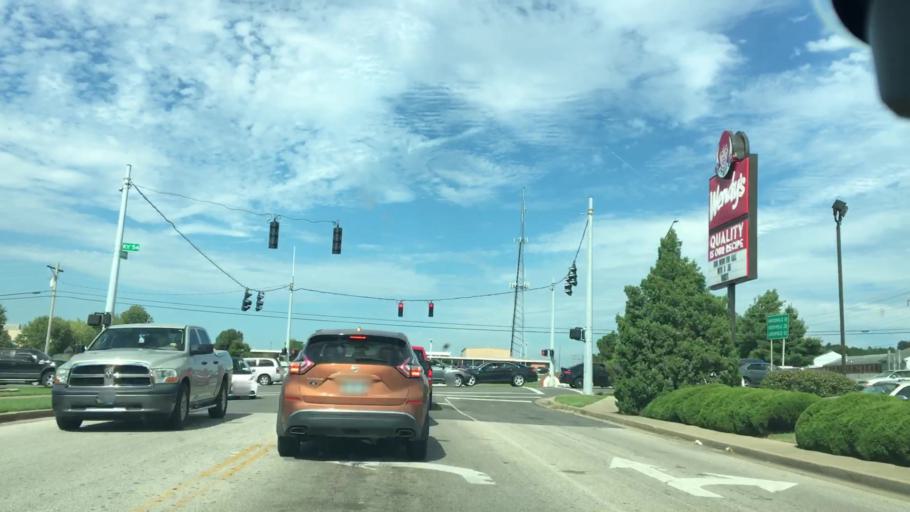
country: US
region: Kentucky
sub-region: Daviess County
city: Owensboro
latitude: 37.7558
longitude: -87.0674
